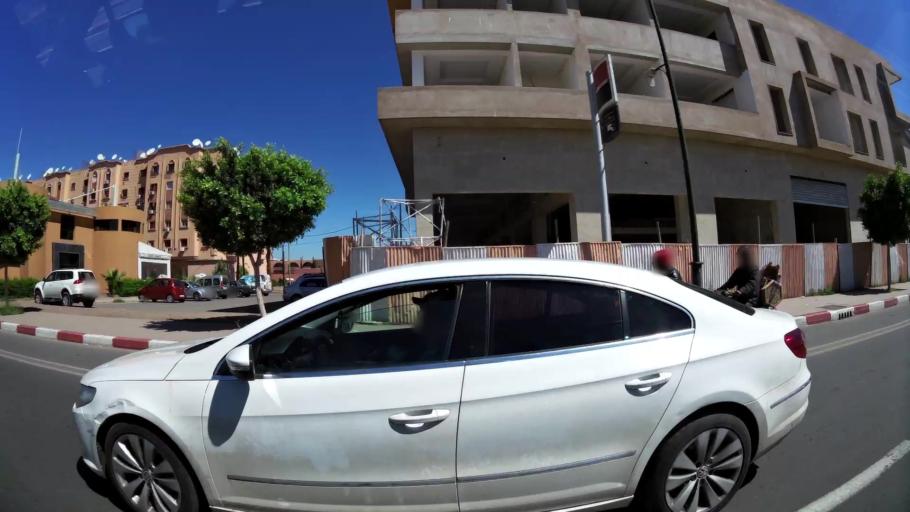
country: MA
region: Marrakech-Tensift-Al Haouz
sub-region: Marrakech
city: Marrakesh
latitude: 31.6278
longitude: -8.0567
